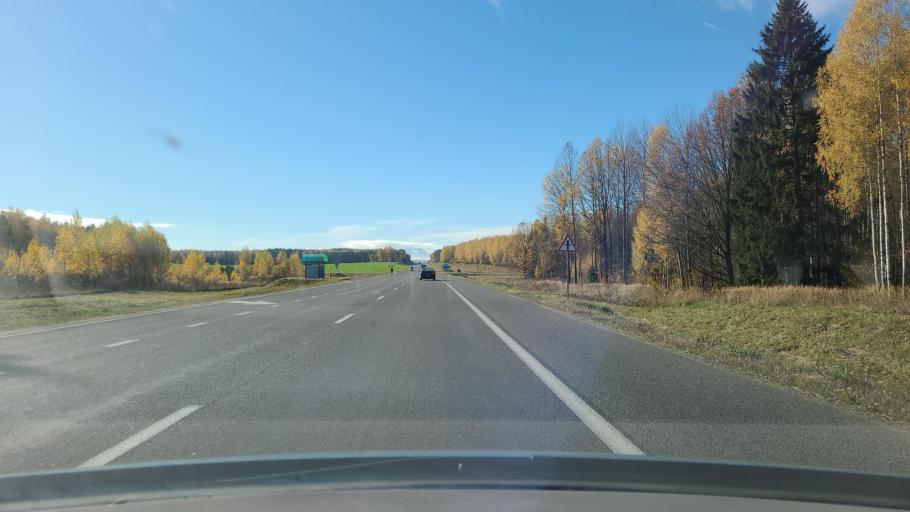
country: BY
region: Grodnenskaya
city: Astravyets
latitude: 54.6556
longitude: 26.0448
